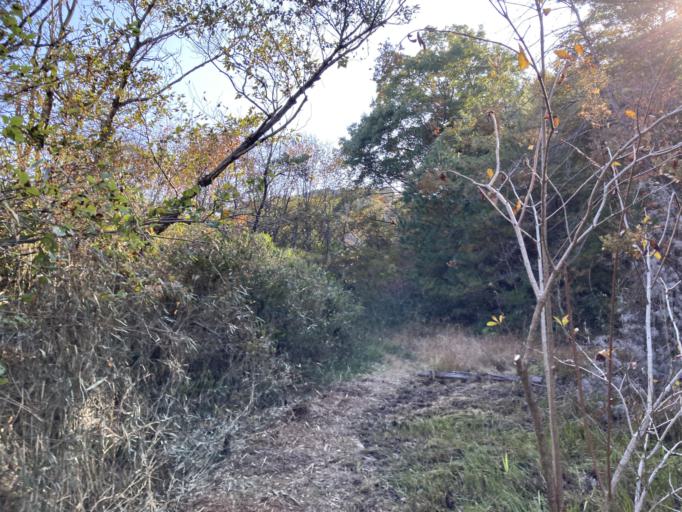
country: JP
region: Nara
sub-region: Ikoma-shi
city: Ikoma
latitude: 34.7021
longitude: 135.6821
